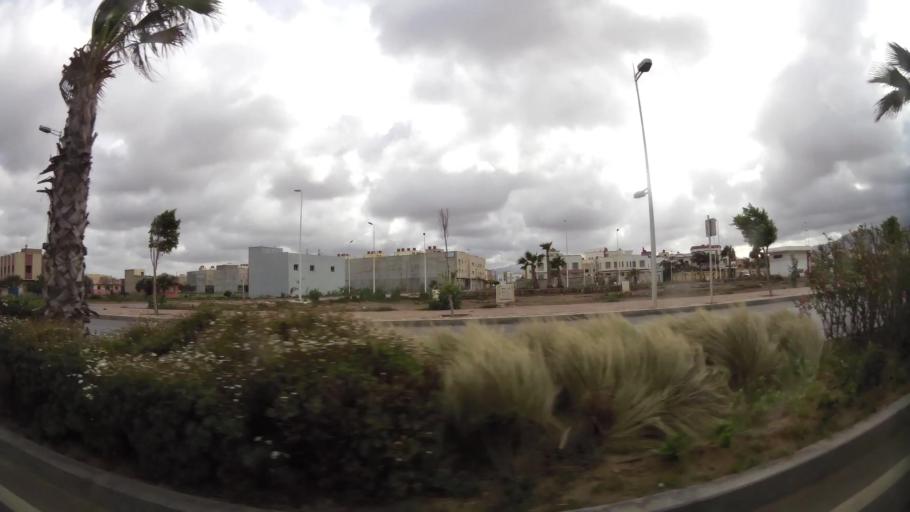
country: MA
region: Oriental
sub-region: Nador
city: Nador
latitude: 35.1649
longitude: -2.9112
